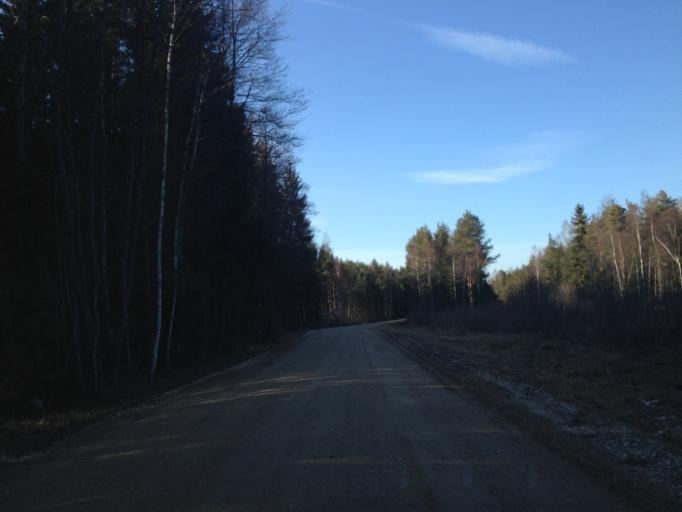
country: EE
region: Harju
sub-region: Nissi vald
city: Turba
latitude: 59.1560
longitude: 24.1443
